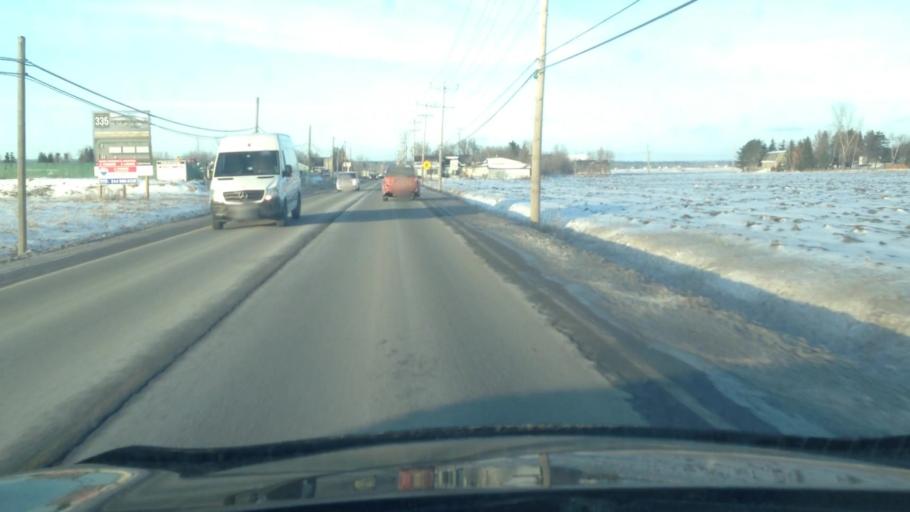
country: CA
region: Quebec
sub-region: Lanaudiere
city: Saint-Lin-Laurentides
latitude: 45.8751
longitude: -73.7574
